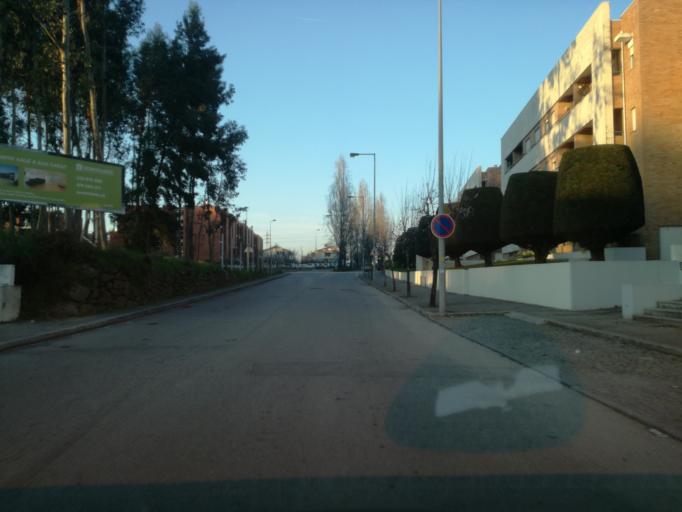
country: PT
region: Porto
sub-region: Maia
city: Milheiros
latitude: 41.2239
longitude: -8.5896
